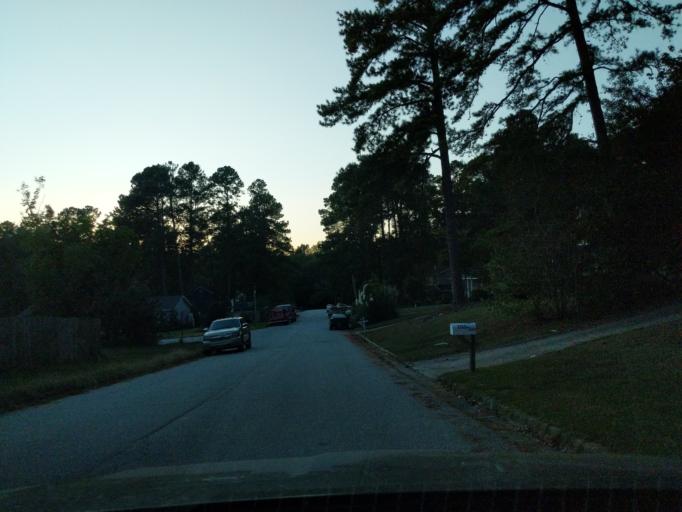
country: US
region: Georgia
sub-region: Columbia County
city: Martinez
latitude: 33.5279
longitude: -82.0897
